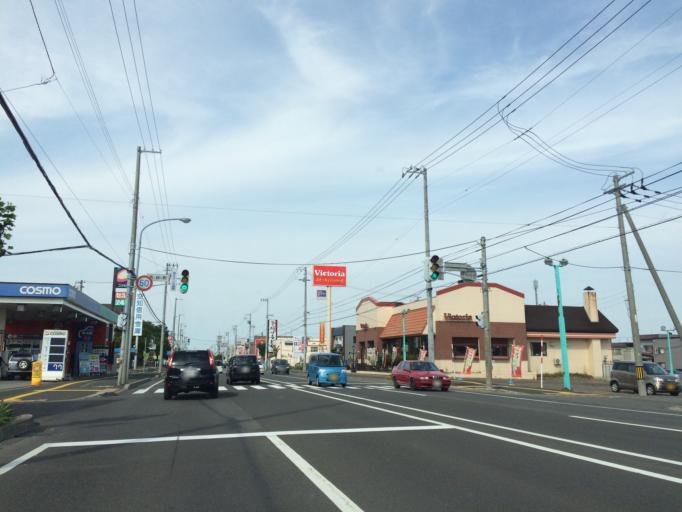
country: JP
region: Hokkaido
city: Ebetsu
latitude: 43.1019
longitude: 141.5361
